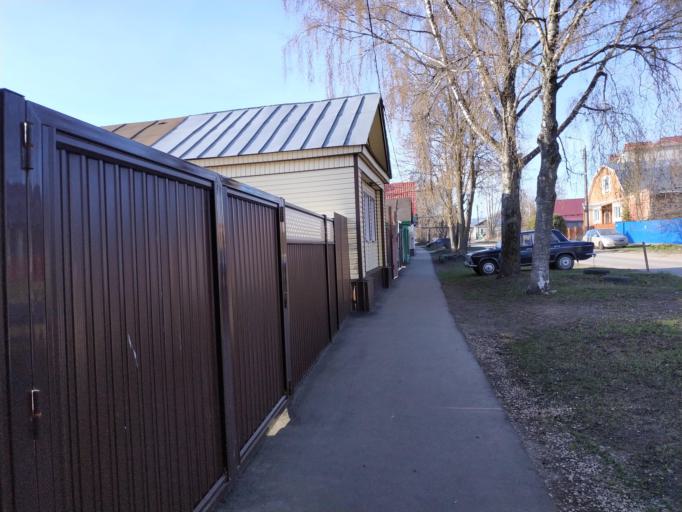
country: RU
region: Nizjnij Novgorod
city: Arzamas
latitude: 55.3958
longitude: 43.8145
